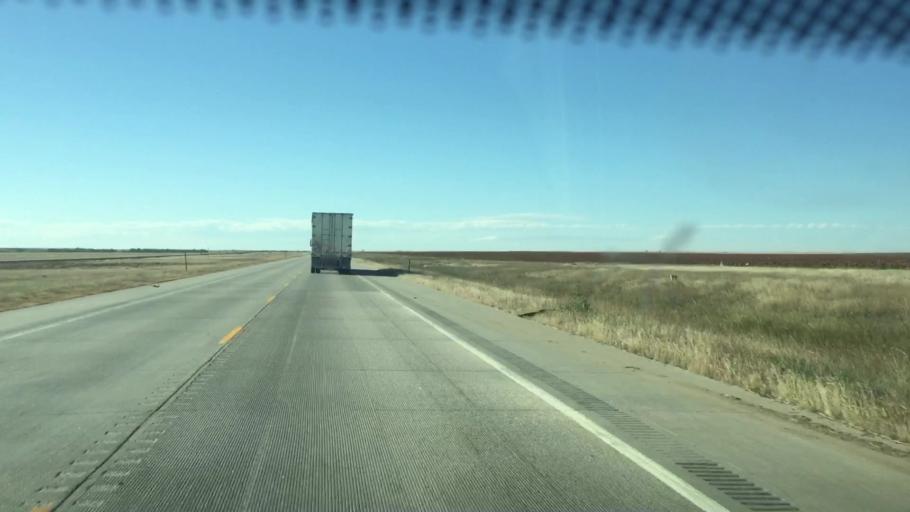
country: US
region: Colorado
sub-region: Kiowa County
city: Eads
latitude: 38.7944
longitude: -102.9428
